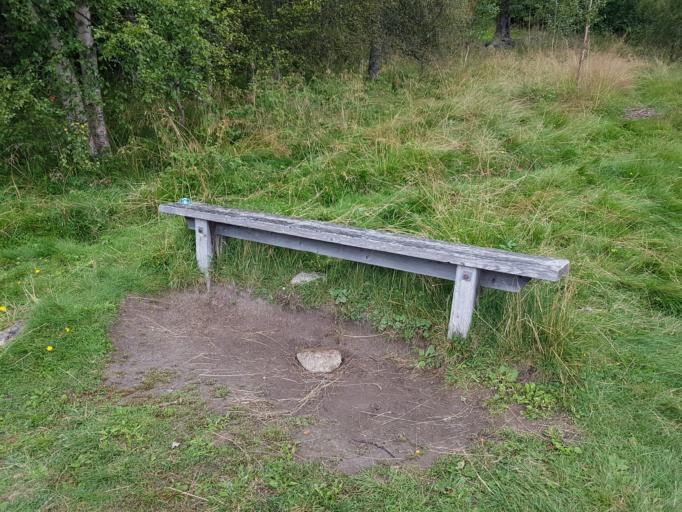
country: NO
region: Sor-Trondelag
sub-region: Trondheim
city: Trondheim
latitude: 63.4212
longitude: 10.3077
